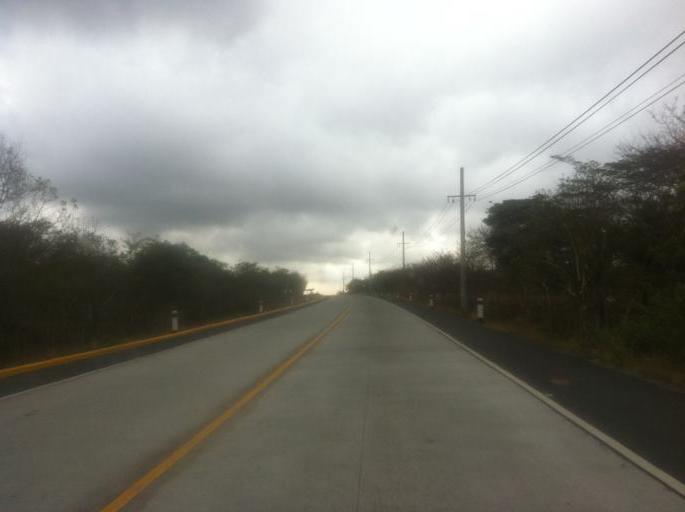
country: NI
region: Masaya
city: Masaya
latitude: 11.9988
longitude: -86.0838
